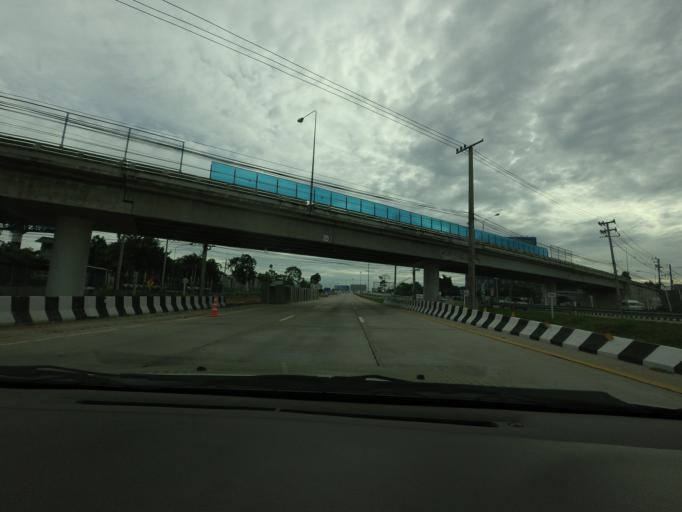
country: TH
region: Chon Buri
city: Phatthaya
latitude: 12.9491
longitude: 100.9347
